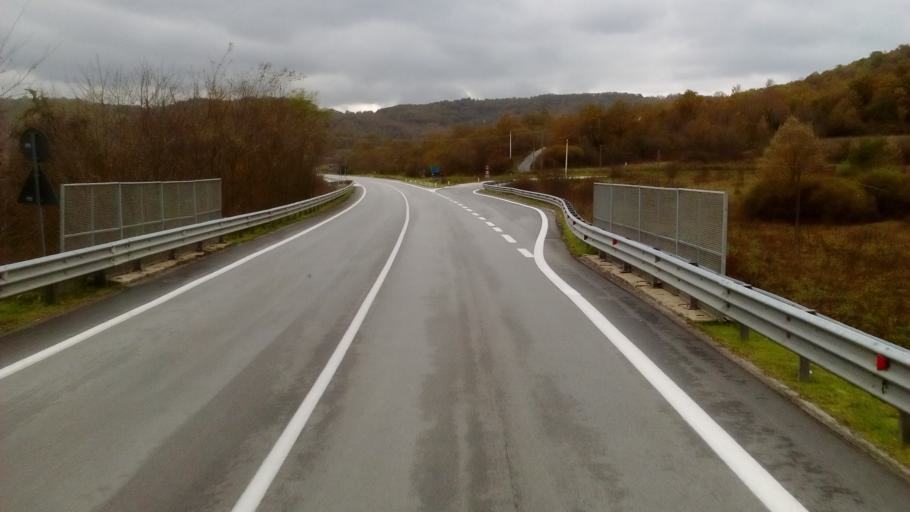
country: IT
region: Molise
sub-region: Provincia di Isernia
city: Sessano del Molise
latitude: 41.6303
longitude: 14.3138
